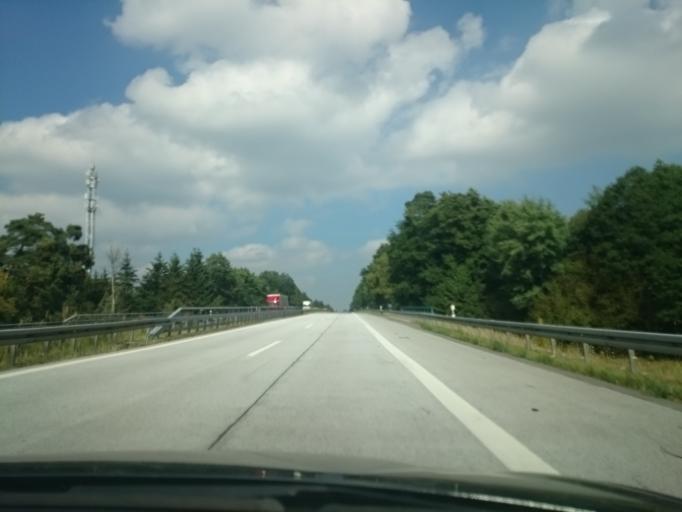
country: DE
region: Brandenburg
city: Althuttendorf
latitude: 53.0208
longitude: 13.8282
